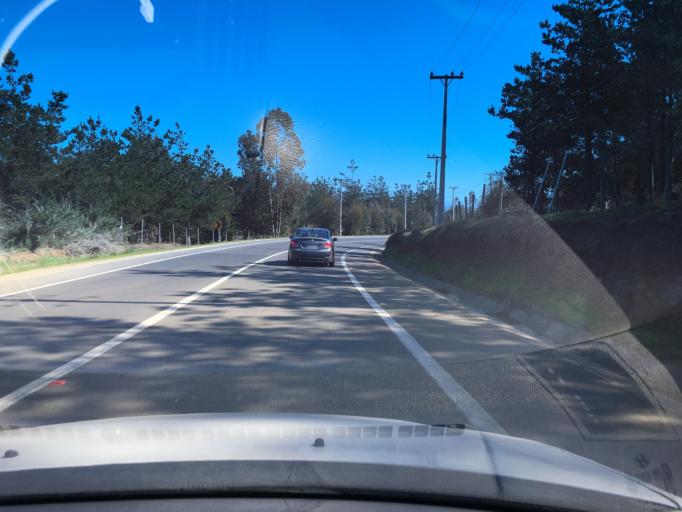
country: CL
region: Valparaiso
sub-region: San Antonio Province
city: El Tabo
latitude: -33.4228
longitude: -71.6798
